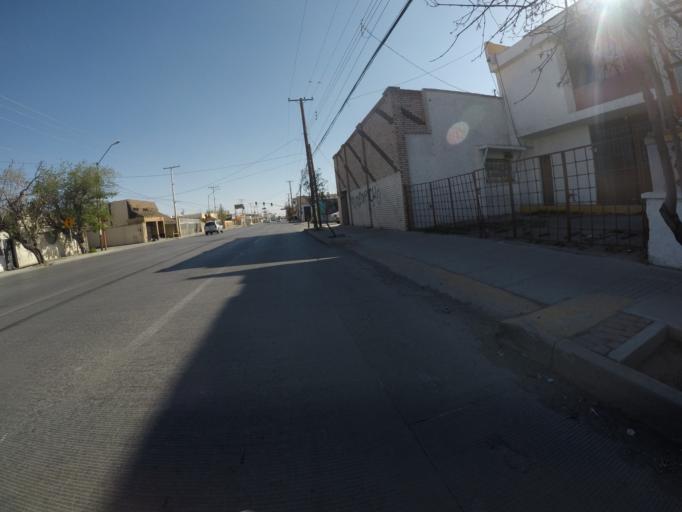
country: MX
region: Chihuahua
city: Ciudad Juarez
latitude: 31.7274
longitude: -106.4505
